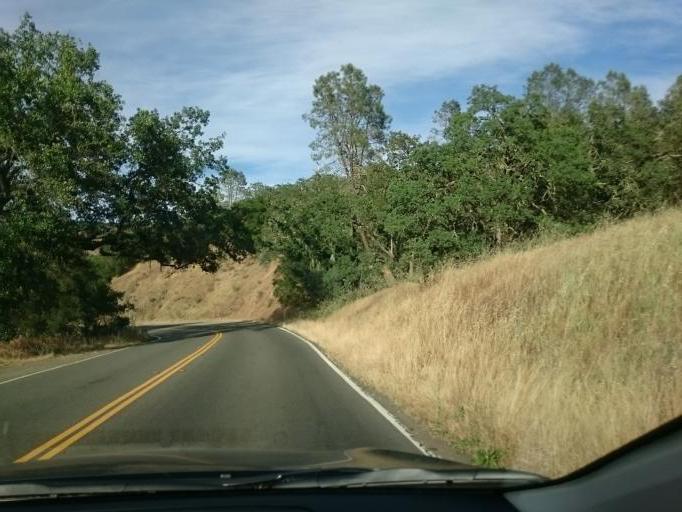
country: US
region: California
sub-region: Napa County
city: Yountville
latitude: 38.4884
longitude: -122.3496
